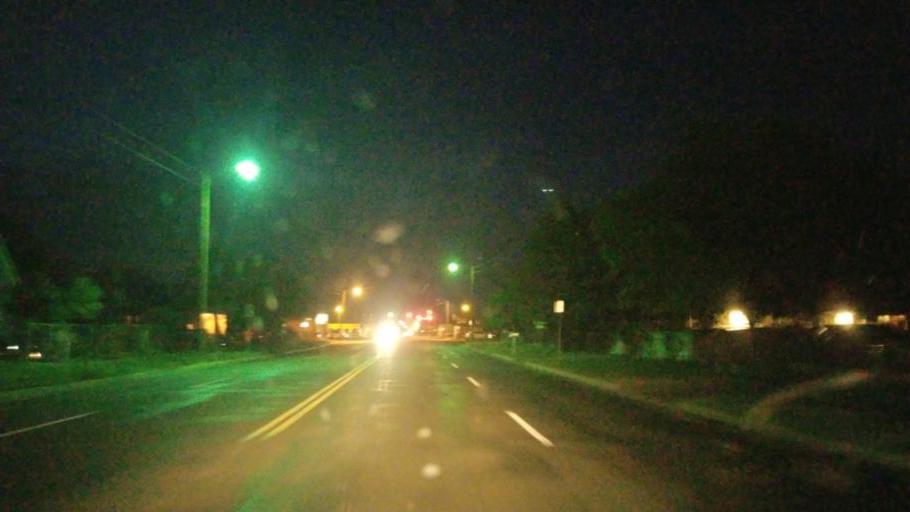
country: US
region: Texas
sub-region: Potter County
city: Amarillo
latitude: 35.1998
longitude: -101.8257
